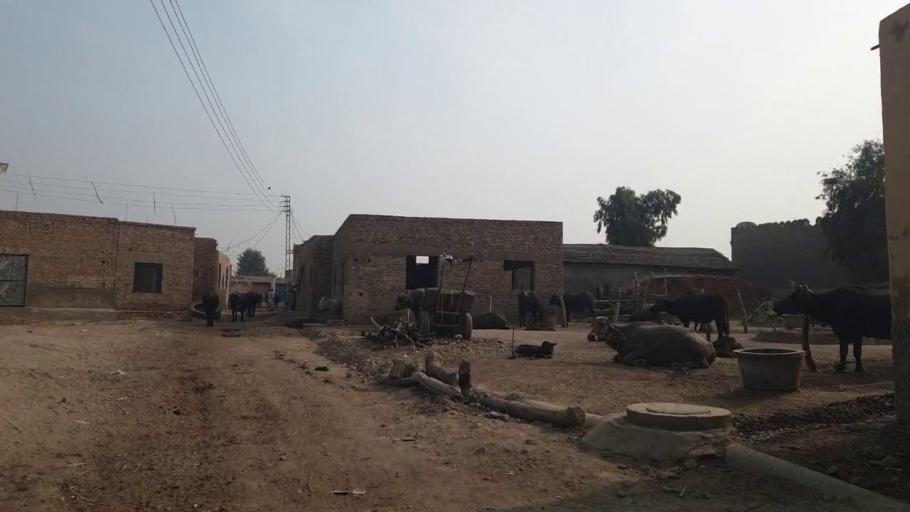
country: PK
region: Sindh
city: Sann
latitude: 26.0689
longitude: 68.1167
